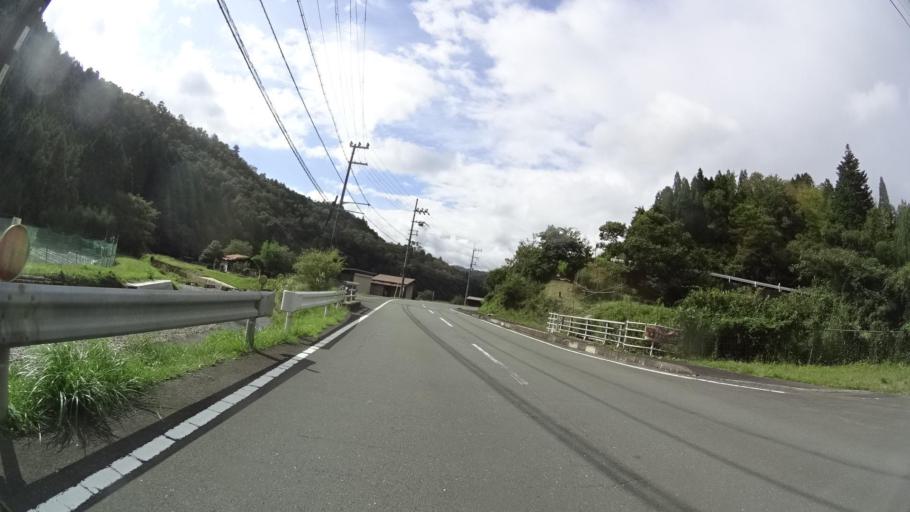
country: JP
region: Kyoto
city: Kameoka
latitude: 35.2071
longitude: 135.5758
